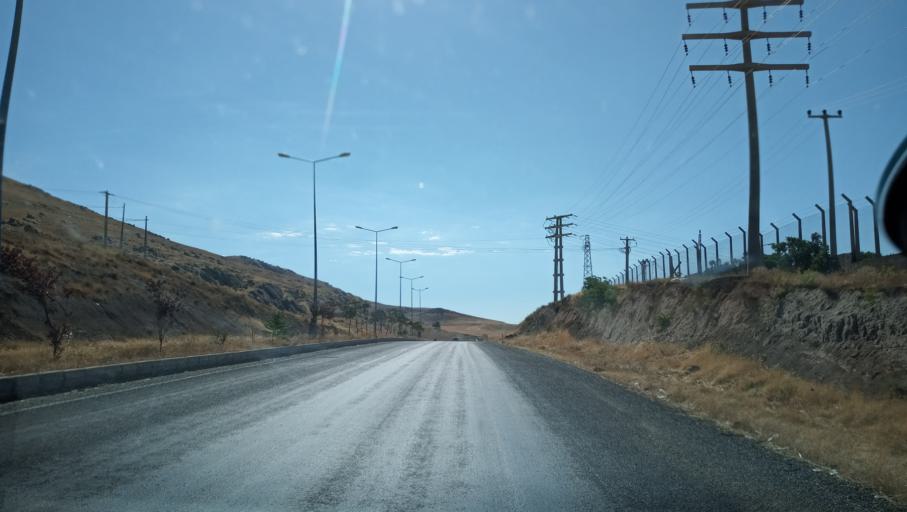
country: TR
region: Diyarbakir
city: Silvan
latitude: 38.1331
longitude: 41.0419
